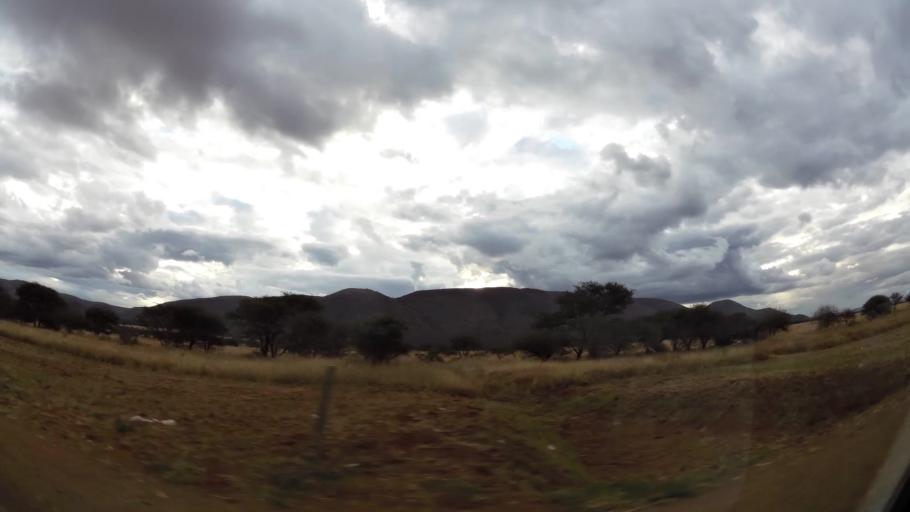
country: ZA
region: Limpopo
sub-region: Waterberg District Municipality
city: Mokopane
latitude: -24.2566
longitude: 28.9877
